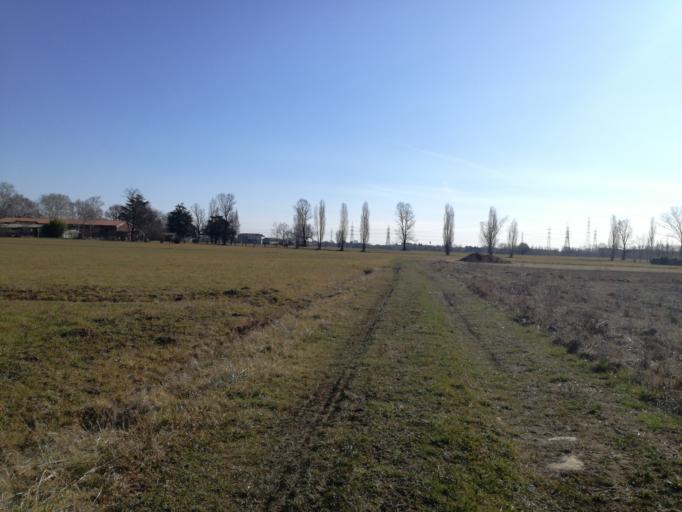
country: IT
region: Lombardy
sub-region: Provincia di Lecco
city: Verderio Inferiore
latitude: 45.6546
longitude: 9.4395
